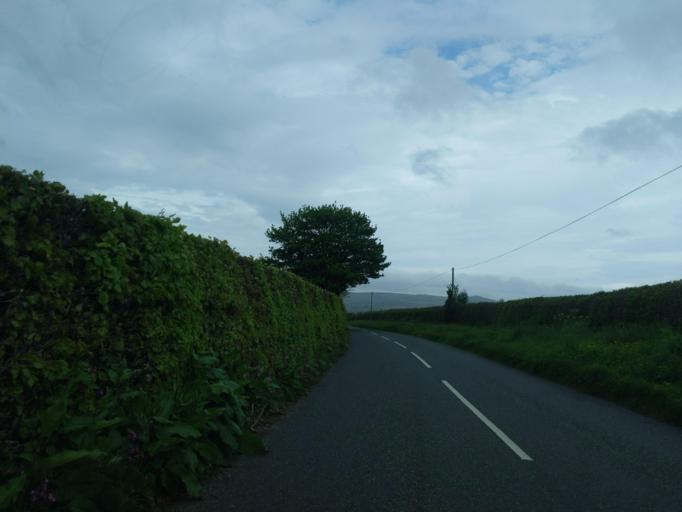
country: GB
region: England
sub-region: Devon
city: Tavistock
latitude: 50.6260
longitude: -4.1361
